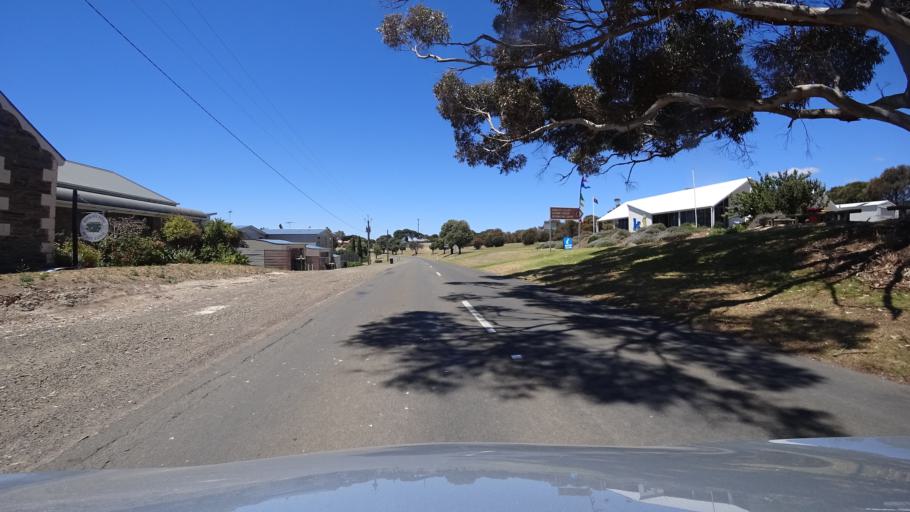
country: AU
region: South Australia
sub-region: Kangaroo Island
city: Kingscote
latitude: -35.7198
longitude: 137.9331
